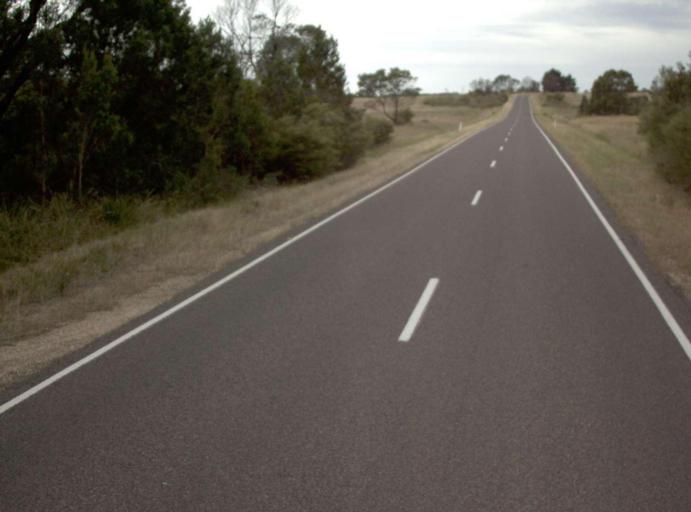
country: AU
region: Victoria
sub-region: East Gippsland
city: Bairnsdale
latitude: -37.9942
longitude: 147.3965
